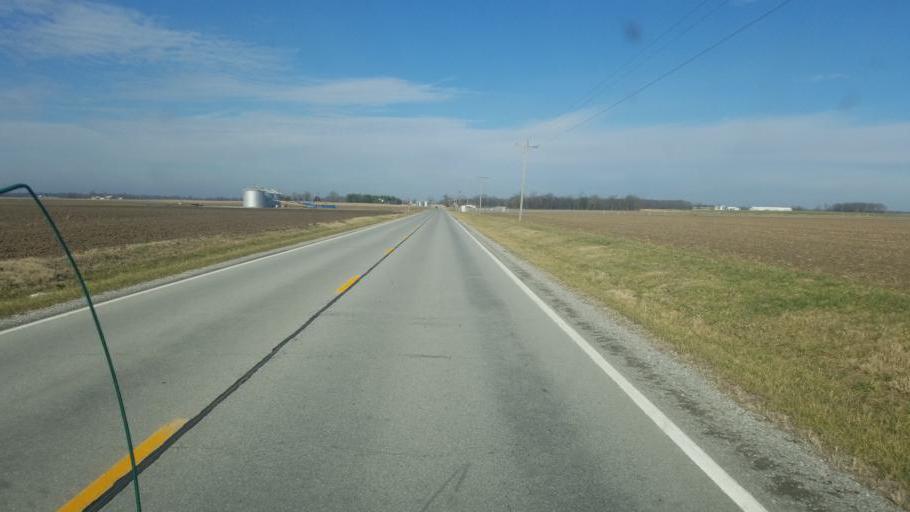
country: US
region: Illinois
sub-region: Saline County
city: Eldorado
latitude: 37.8896
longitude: -88.4530
